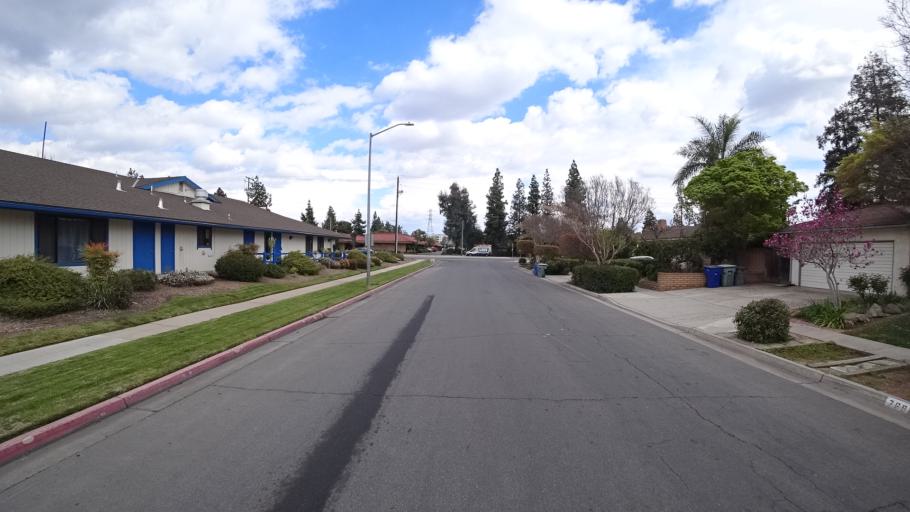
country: US
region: California
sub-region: Fresno County
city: Clovis
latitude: 36.8357
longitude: -119.7731
